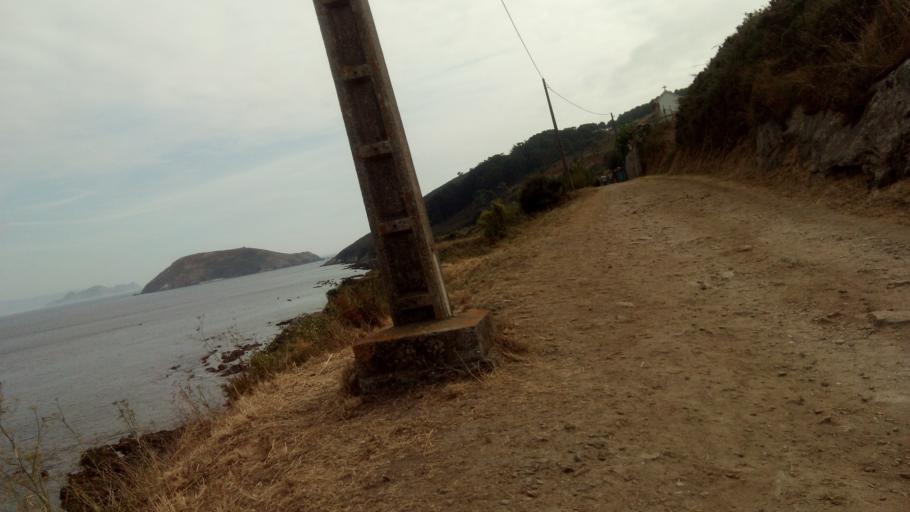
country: ES
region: Galicia
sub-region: Provincia de Pontevedra
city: Sanxenxo
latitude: 42.3669
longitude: -8.9348
